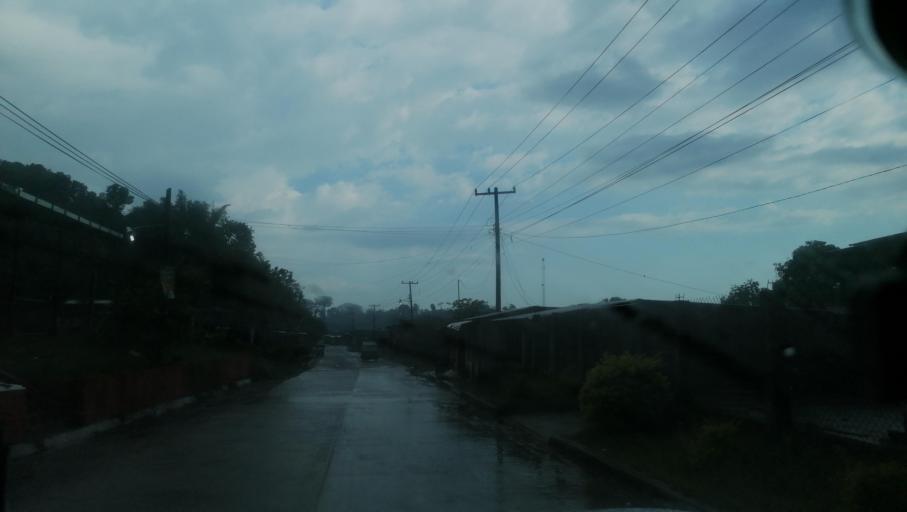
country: MX
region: Chiapas
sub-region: Cacahoatan
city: Benito Juarez
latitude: 15.0553
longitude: -92.1914
